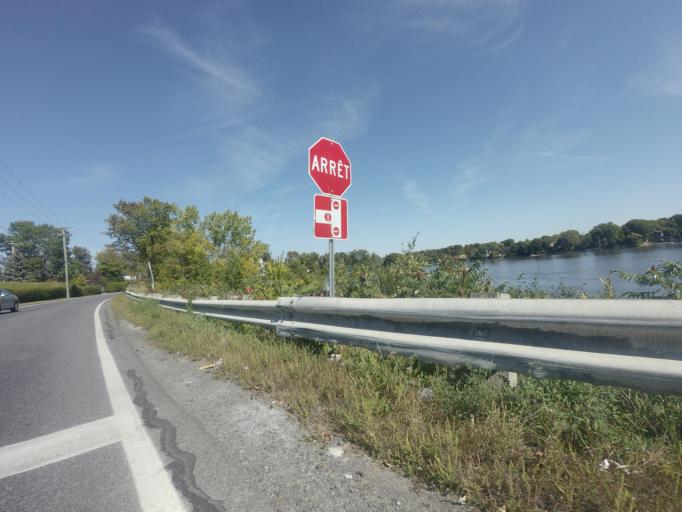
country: CA
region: Quebec
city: Dollard-Des Ormeaux
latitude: 45.5023
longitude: -73.8636
